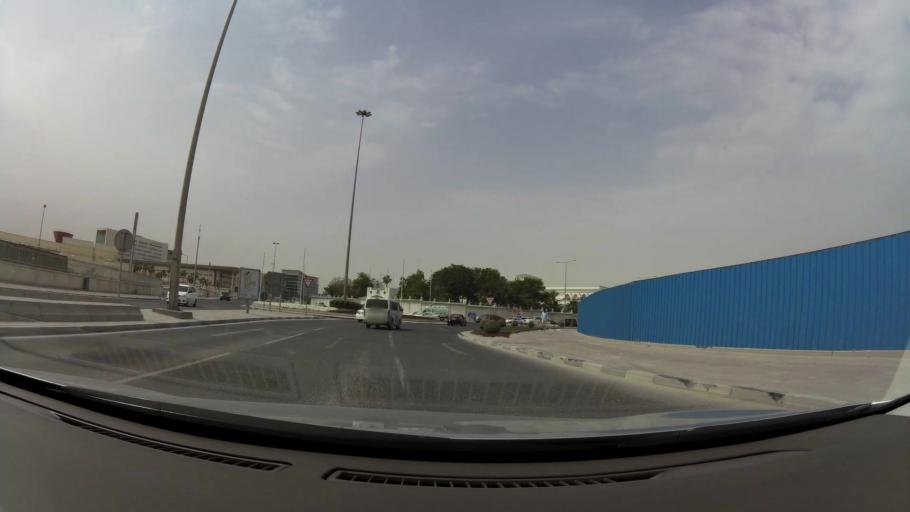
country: QA
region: Baladiyat ad Dawhah
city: Doha
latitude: 25.2933
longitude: 51.5143
